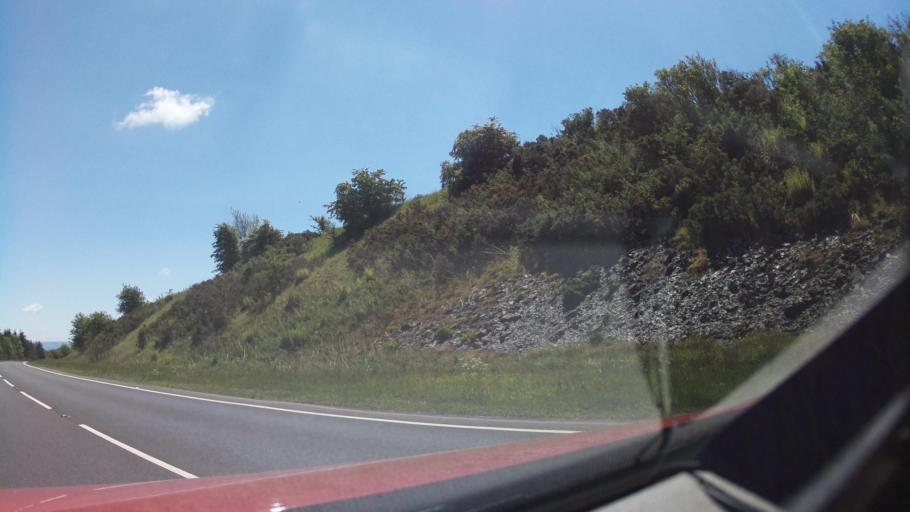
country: GB
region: Scotland
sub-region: The Scottish Borders
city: Hawick
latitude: 55.4728
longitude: -2.7974
